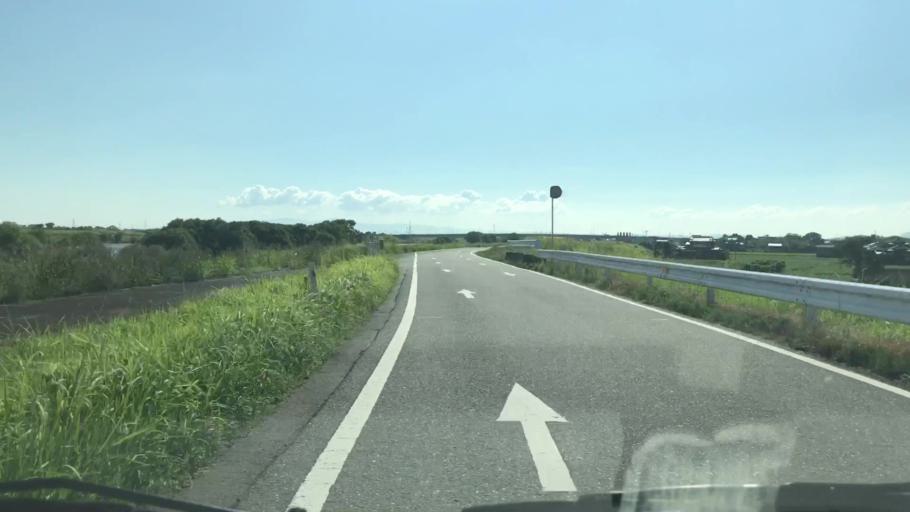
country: JP
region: Saga Prefecture
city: Kanzakimachi-kanzaki
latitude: 33.2755
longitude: 130.4423
